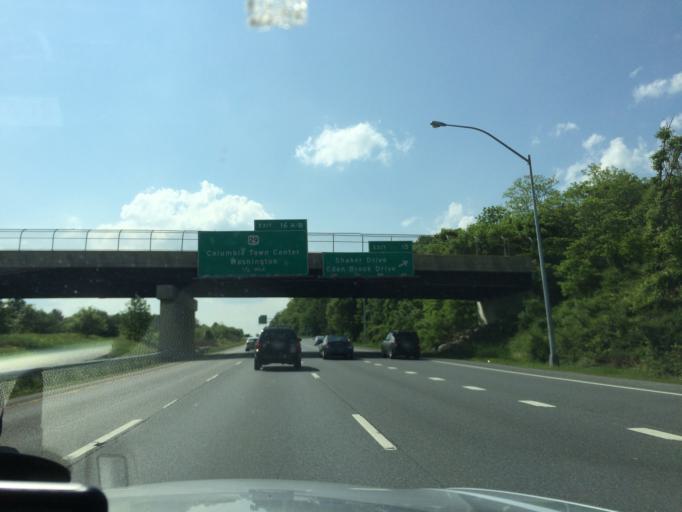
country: US
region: Maryland
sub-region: Howard County
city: Riverside
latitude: 39.1765
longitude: -76.8588
